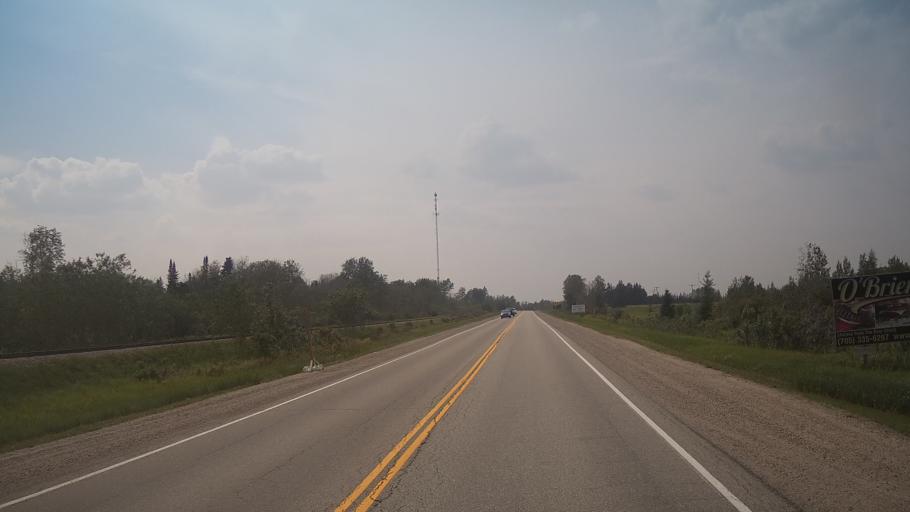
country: CA
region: Ontario
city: Kapuskasing
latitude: 49.3893
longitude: -82.3473
